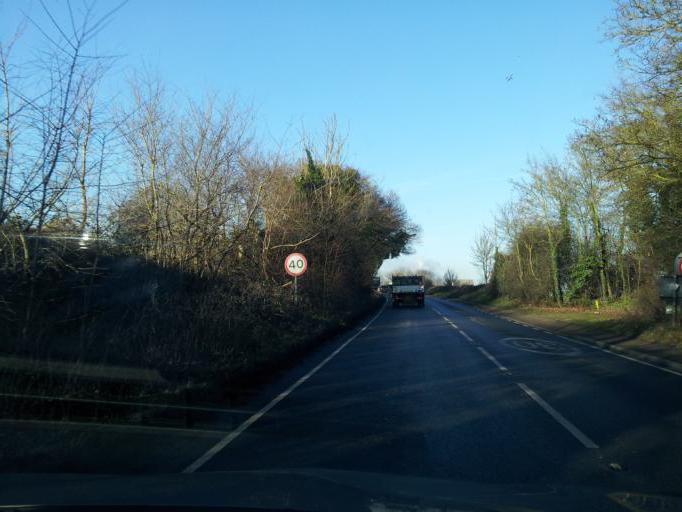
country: GB
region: England
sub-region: Suffolk
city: Bury St Edmunds
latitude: 52.2143
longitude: 0.7456
